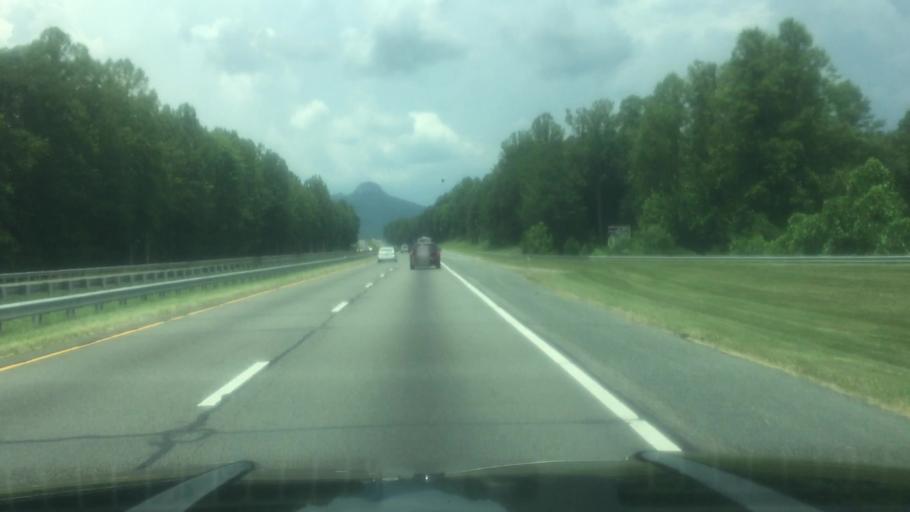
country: US
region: North Carolina
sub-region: Stokes County
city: King
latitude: 36.3076
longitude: -80.4233
